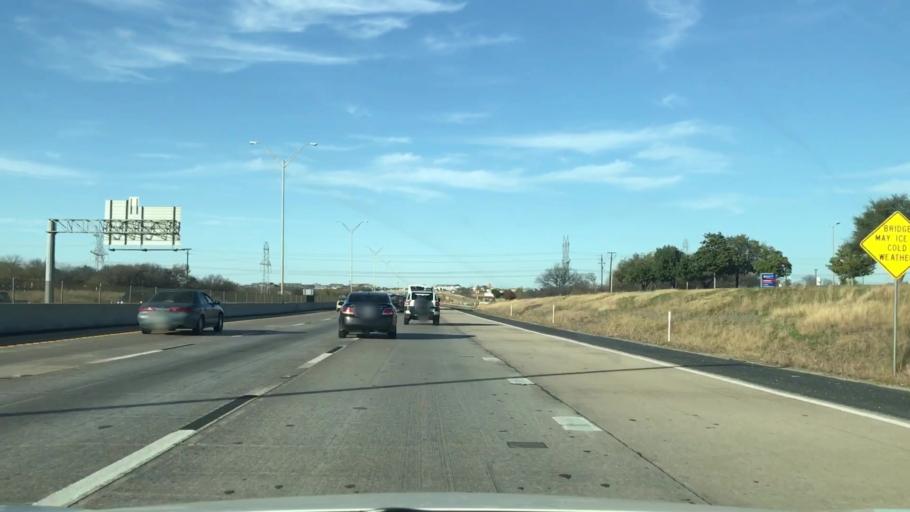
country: US
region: Texas
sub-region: Tarrant County
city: Crowley
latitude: 32.5856
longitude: -97.3195
